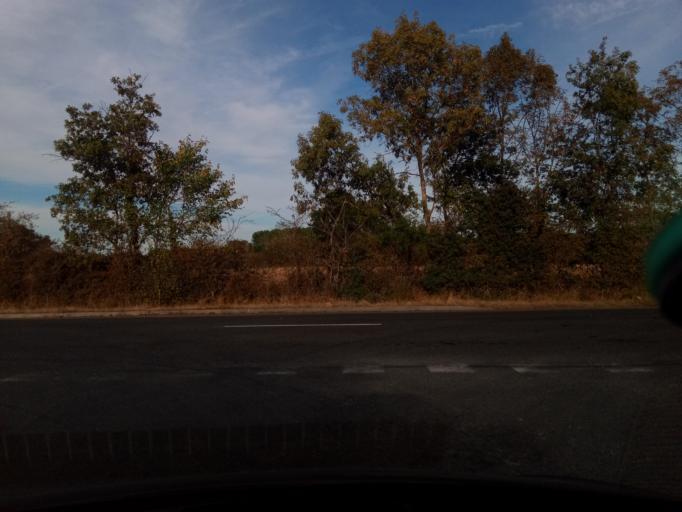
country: FR
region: Poitou-Charentes
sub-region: Departement de la Vienne
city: Saulge
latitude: 46.4022
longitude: 0.8944
